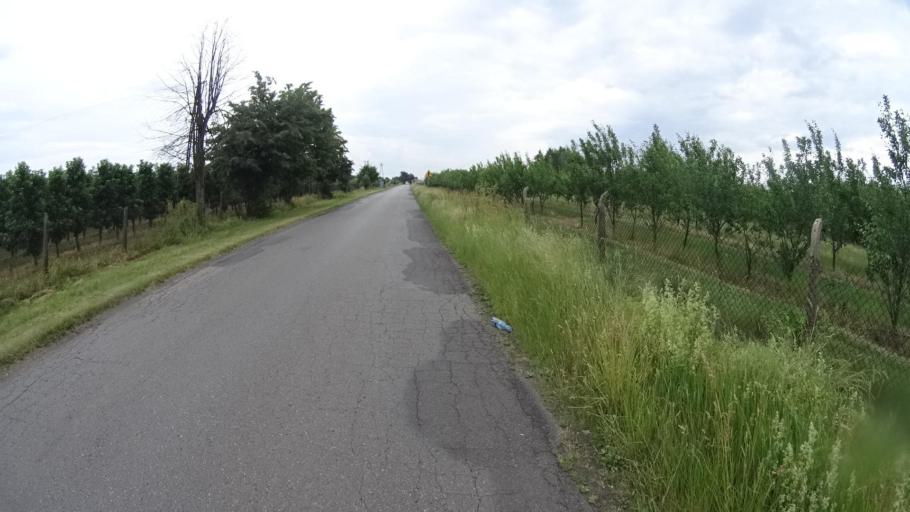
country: PL
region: Masovian Voivodeship
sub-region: Powiat grojecki
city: Goszczyn
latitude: 51.7739
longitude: 20.8534
